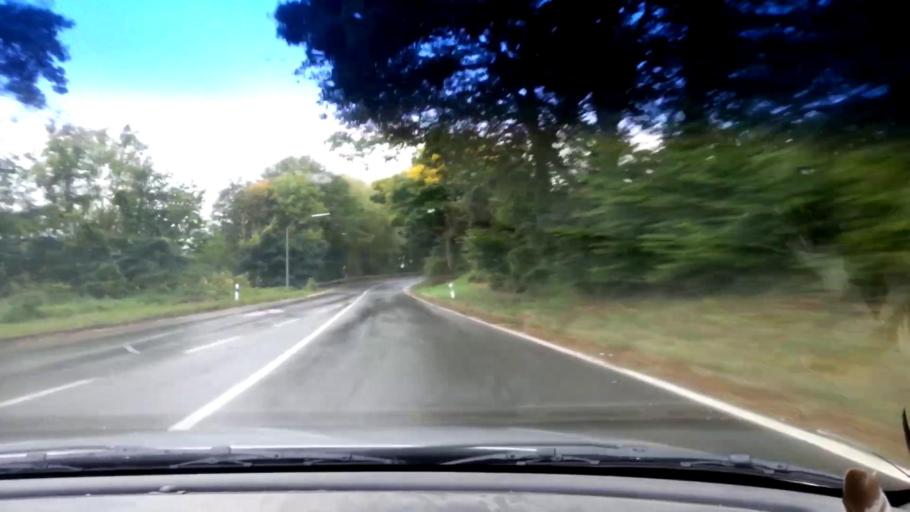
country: DE
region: Bavaria
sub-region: Upper Franconia
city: Schesslitz
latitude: 49.9805
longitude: 11.0843
